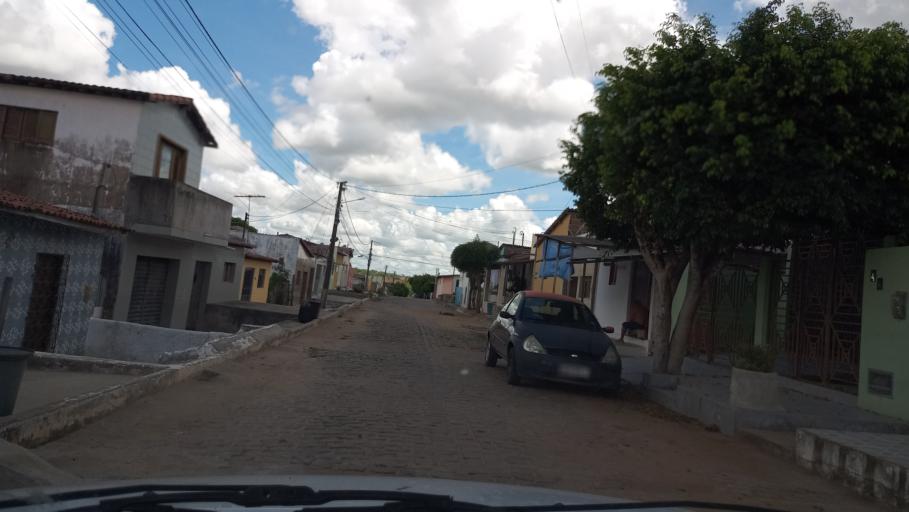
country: BR
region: Rio Grande do Norte
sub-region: Sao Paulo Do Potengi
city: Sao Paulo do Potengi
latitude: -5.8979
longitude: -35.7707
